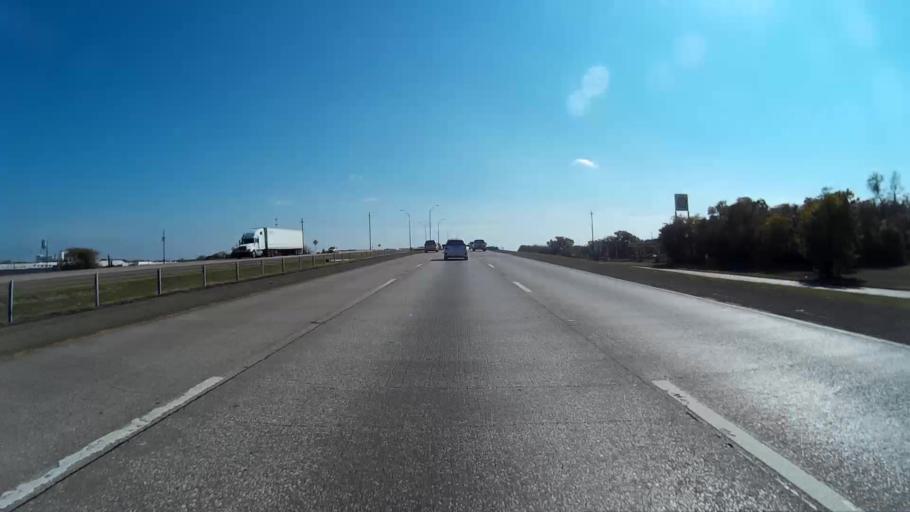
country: US
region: Texas
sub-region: Dallas County
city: Hutchins
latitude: 32.7162
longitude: -96.7582
